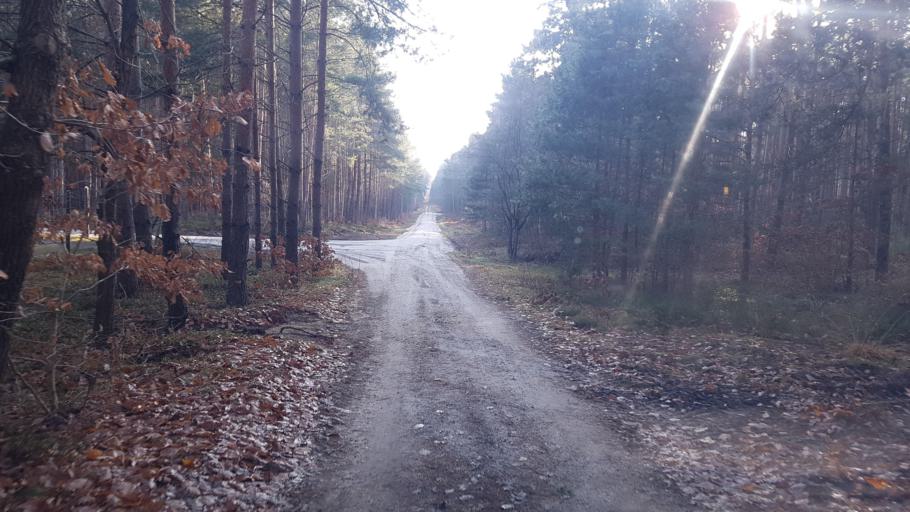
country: DE
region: Brandenburg
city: Plessa
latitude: 51.5262
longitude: 13.6714
